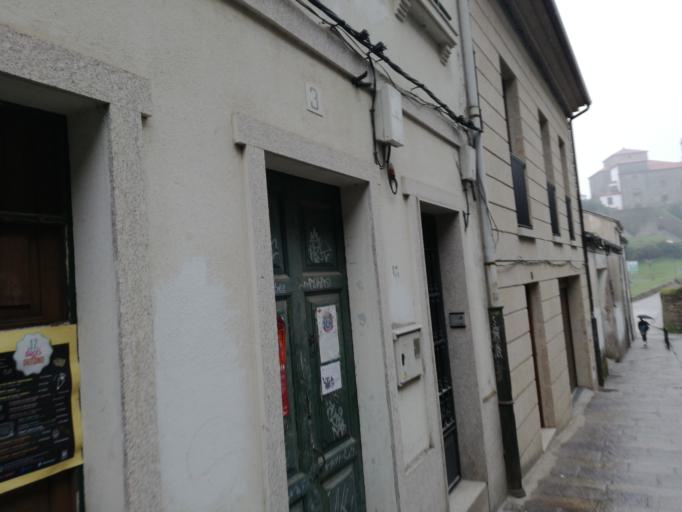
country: ES
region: Galicia
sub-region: Provincia da Coruna
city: Santiago de Compostela
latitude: 42.8789
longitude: -8.5398
